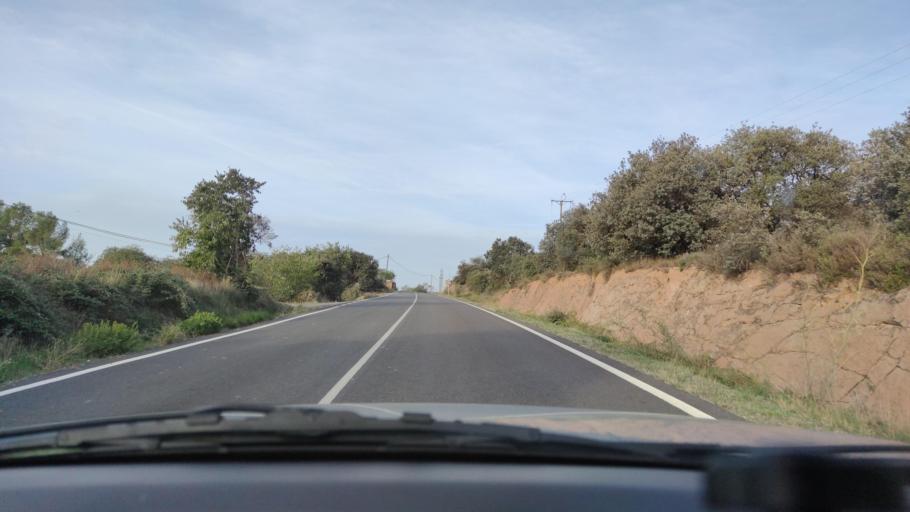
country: ES
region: Catalonia
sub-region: Provincia de Lleida
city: Artesa de Segre
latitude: 41.8479
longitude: 1.0551
